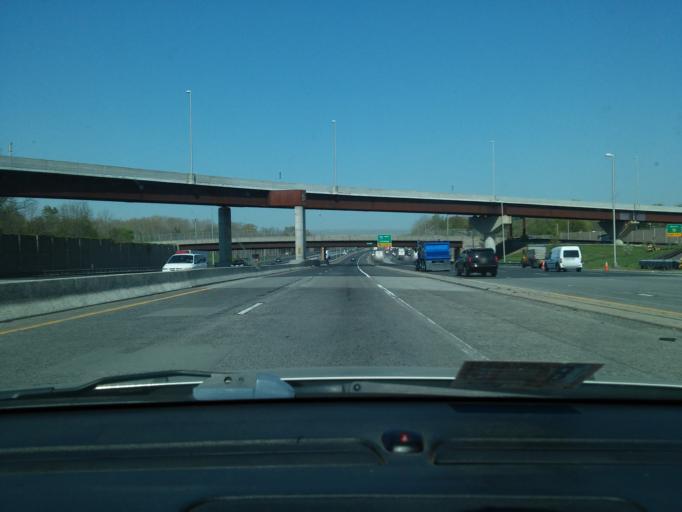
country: US
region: New Jersey
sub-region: Union County
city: Union
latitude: 40.7060
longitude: -74.2493
